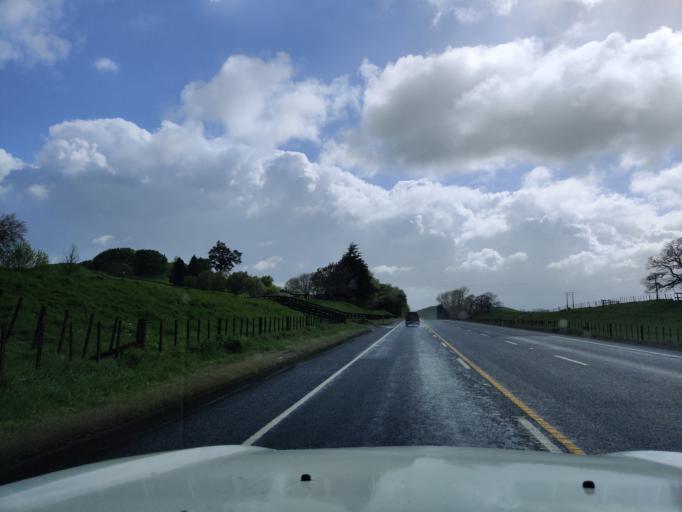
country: NZ
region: Waikato
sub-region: Matamata-Piako District
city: Matamata
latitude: -37.9817
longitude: 175.7359
